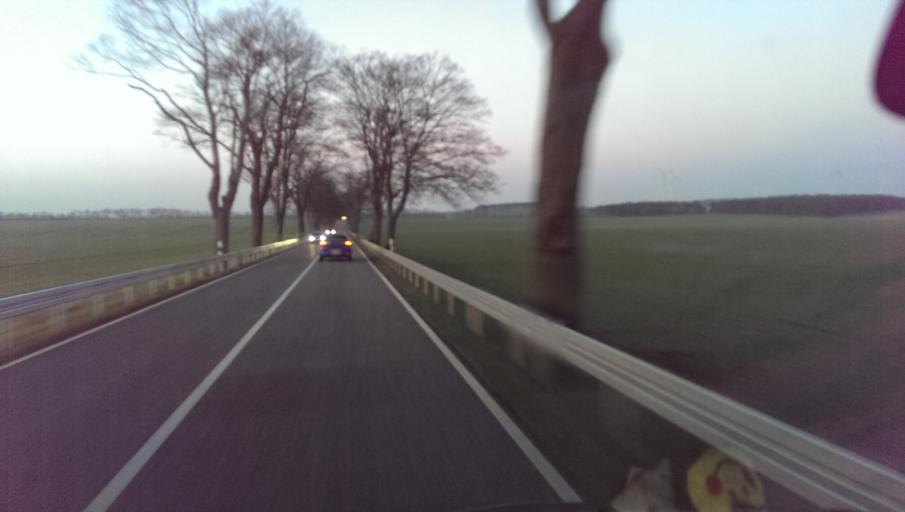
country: DE
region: Brandenburg
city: Juterbog
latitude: 51.9480
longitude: 13.1166
